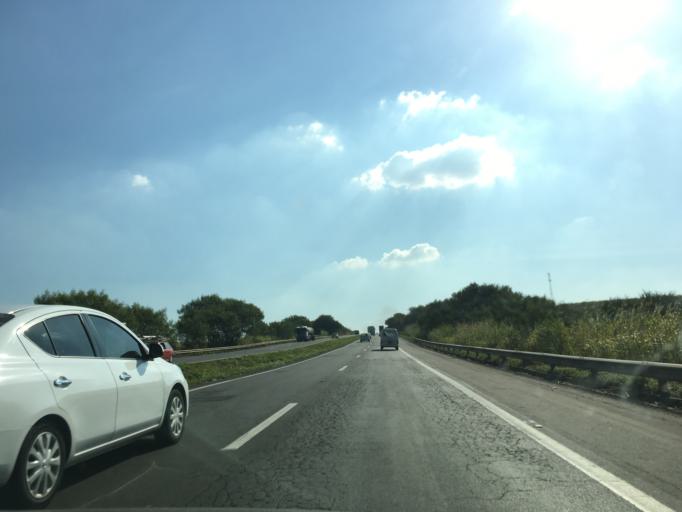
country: BR
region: Sao Paulo
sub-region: Santa Barbara D'Oeste
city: Santa Barbara d'Oeste
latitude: -22.7520
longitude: -47.4907
